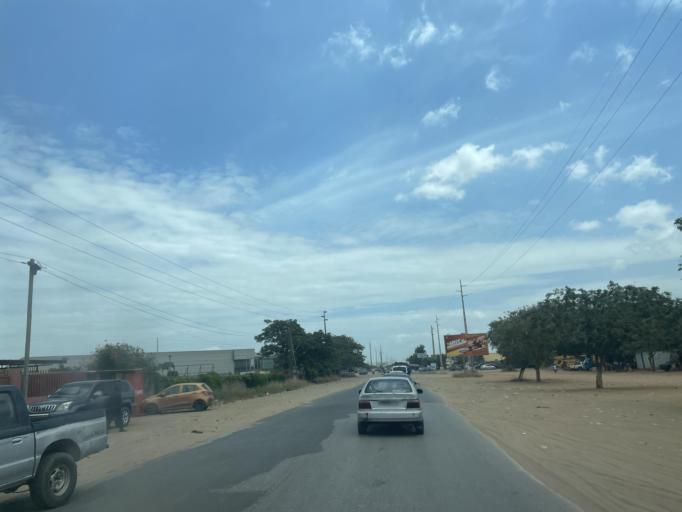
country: AO
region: Luanda
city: Luanda
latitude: -8.9437
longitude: 13.3842
